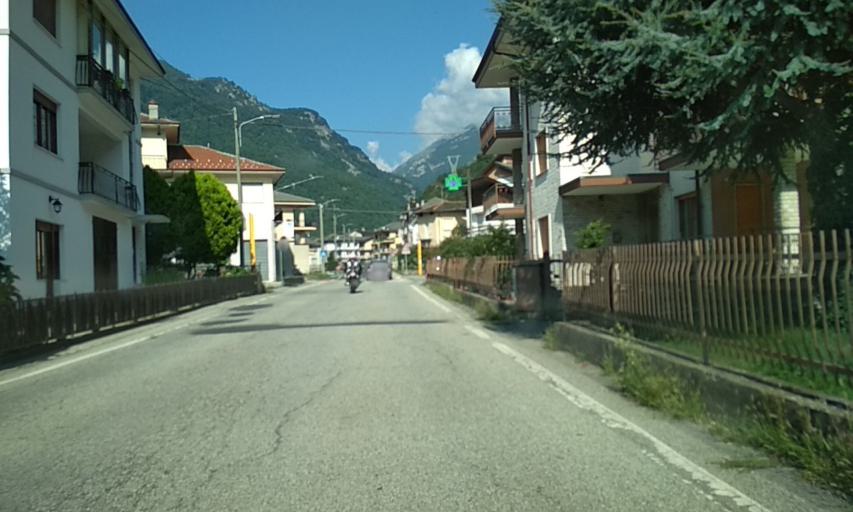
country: IT
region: Piedmont
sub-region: Provincia di Torino
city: Locana
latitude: 45.4171
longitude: 7.4570
